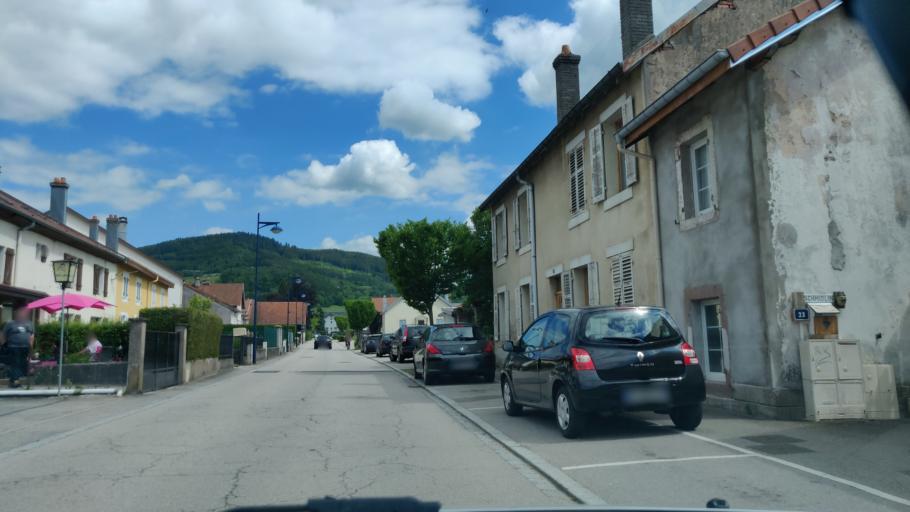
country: FR
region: Lorraine
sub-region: Departement des Vosges
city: Fraize
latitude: 48.1853
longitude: 7.0043
